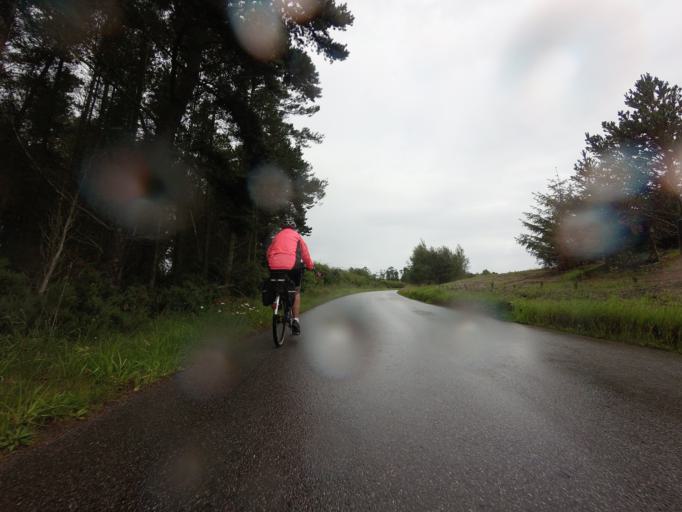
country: GB
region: Scotland
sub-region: Moray
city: Fochabers
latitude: 57.6610
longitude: -3.0662
